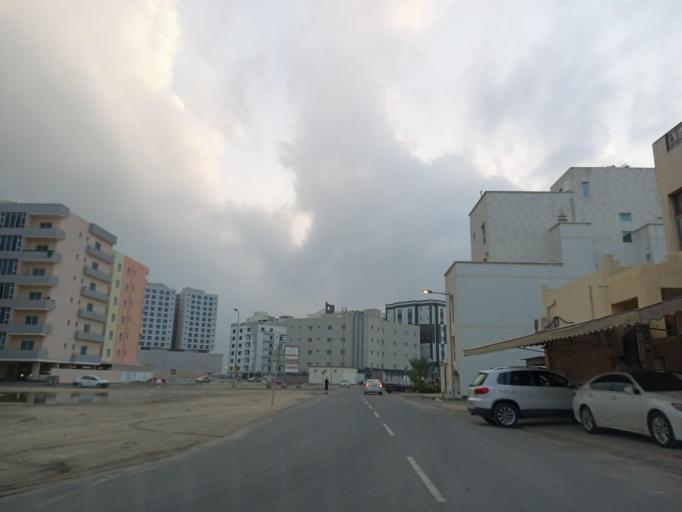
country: BH
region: Muharraq
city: Al Hadd
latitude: 26.2298
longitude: 50.6548
